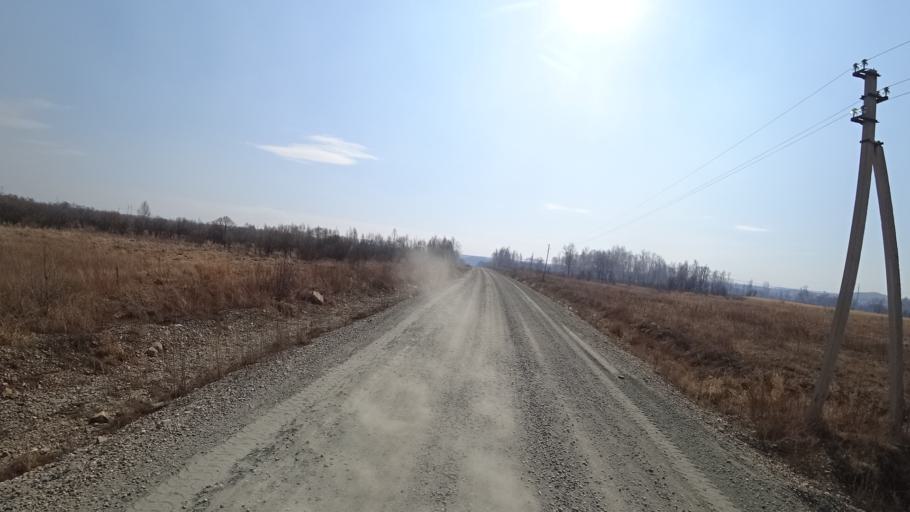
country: RU
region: Amur
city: Novobureyskiy
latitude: 49.8065
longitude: 129.9650
